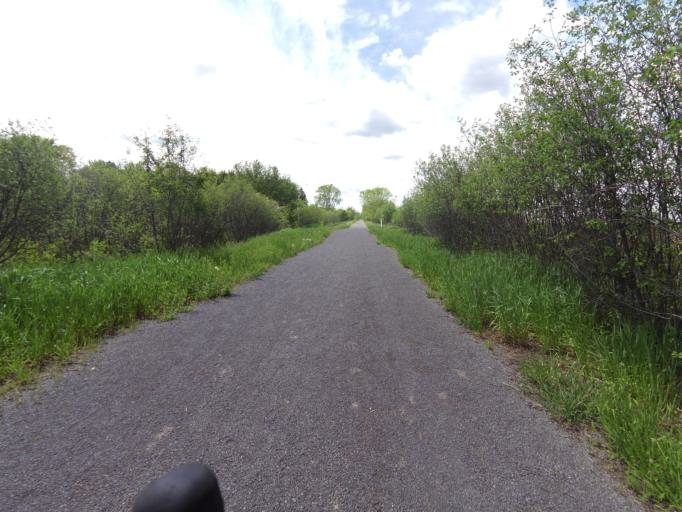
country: CA
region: Ontario
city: Ottawa
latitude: 45.4159
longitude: -75.5735
